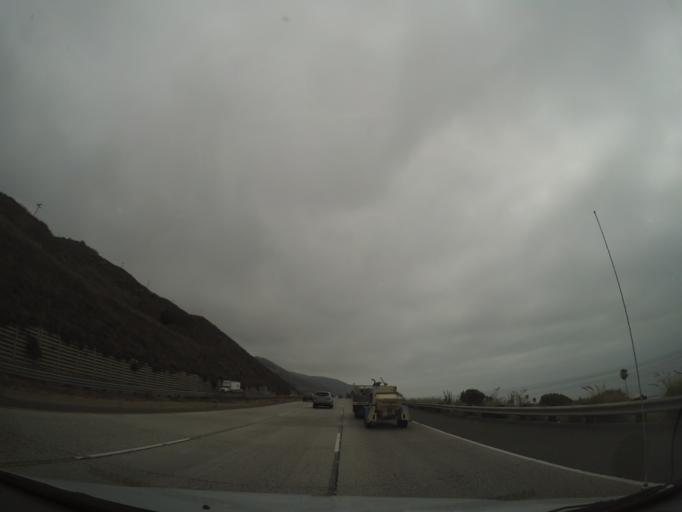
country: US
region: California
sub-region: Ventura County
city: Ventura
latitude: 34.3160
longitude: -119.3623
